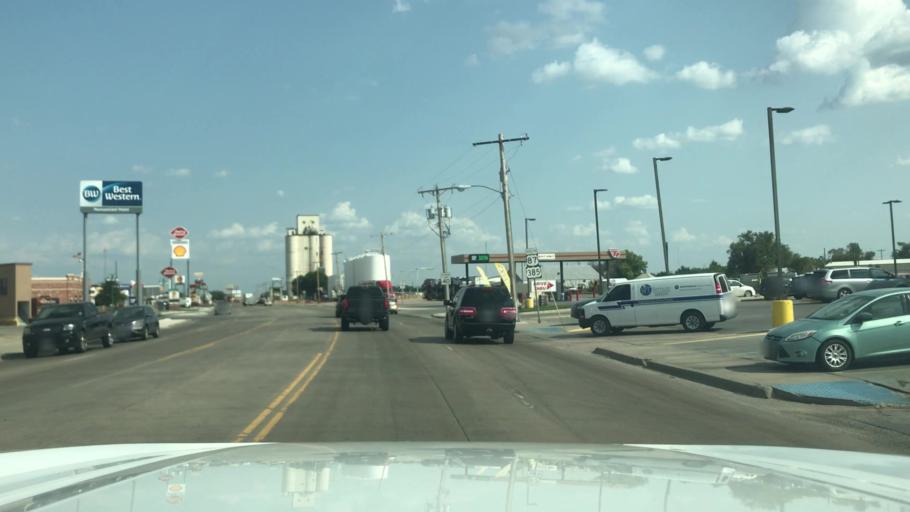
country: US
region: Texas
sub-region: Dallam County
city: Dalhart
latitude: 36.0648
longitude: -102.5206
